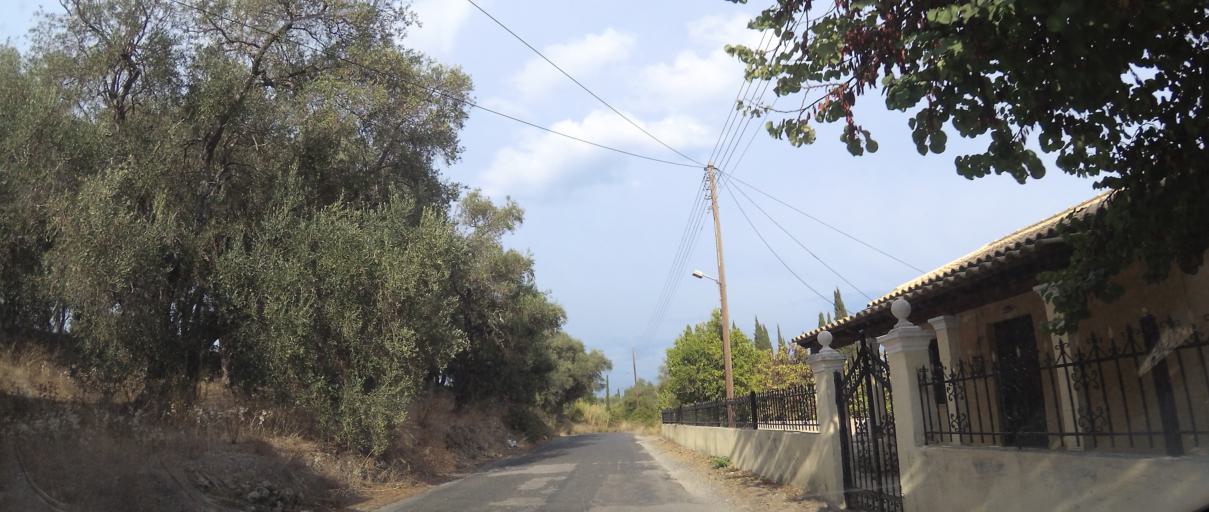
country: GR
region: Ionian Islands
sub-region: Nomos Kerkyras
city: Kynopiastes
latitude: 39.5621
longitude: 19.8640
